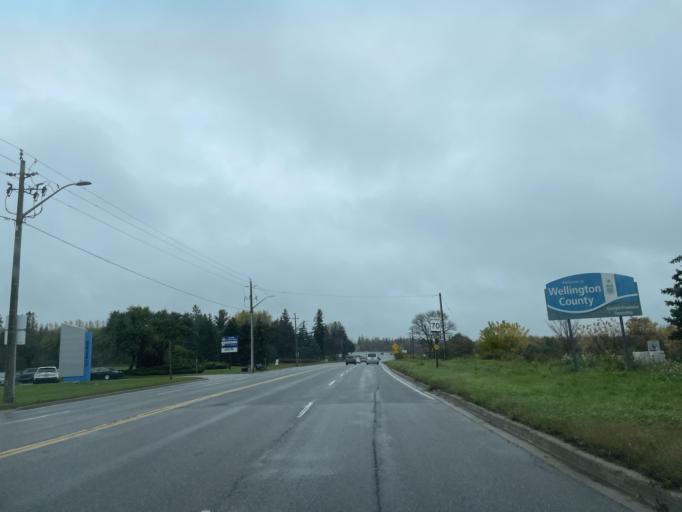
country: CA
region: Ontario
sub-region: Wellington County
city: Guelph
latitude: 43.5668
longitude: -80.2782
